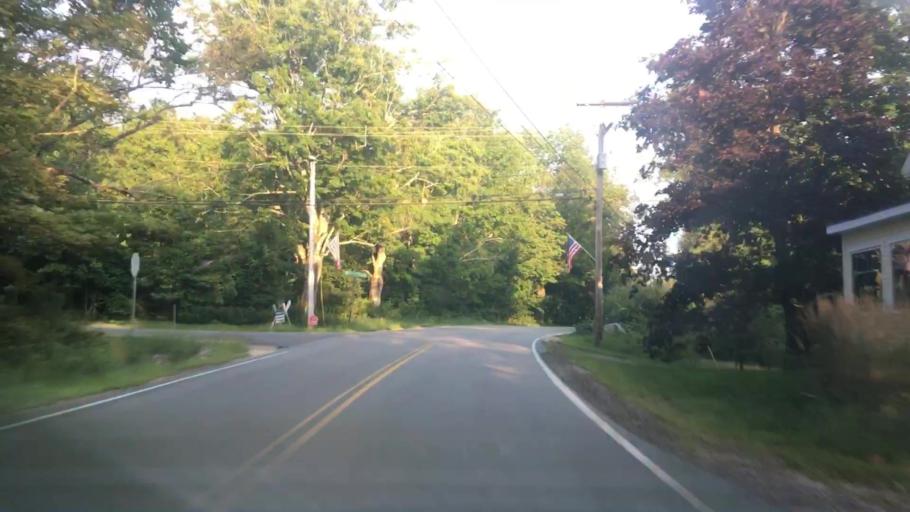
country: US
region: New Hampshire
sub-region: Belknap County
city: Barnstead
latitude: 43.4205
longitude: -71.3018
